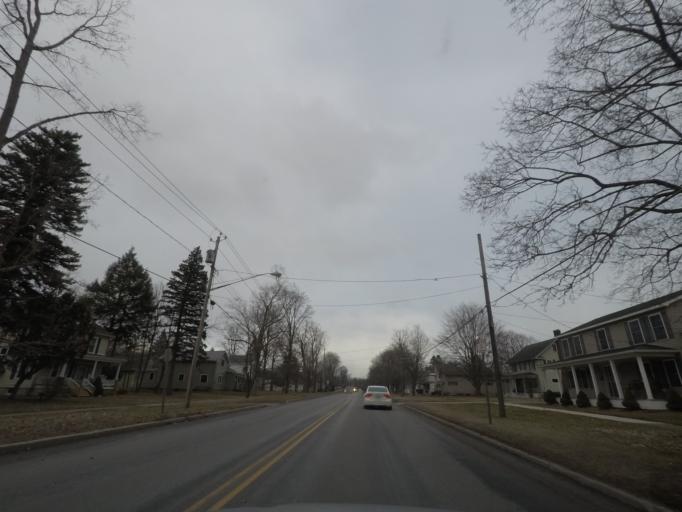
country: US
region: New York
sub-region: Madison County
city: Oneida
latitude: 43.0777
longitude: -75.6316
